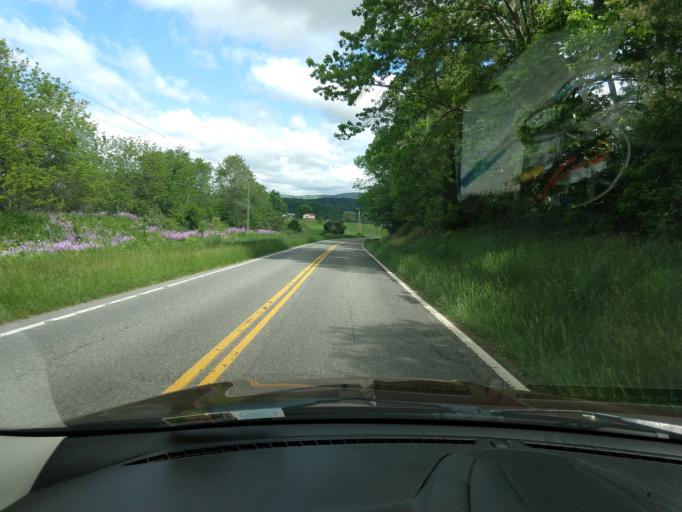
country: US
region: Virginia
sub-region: Wythe County
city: Wytheville
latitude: 36.8499
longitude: -80.9754
